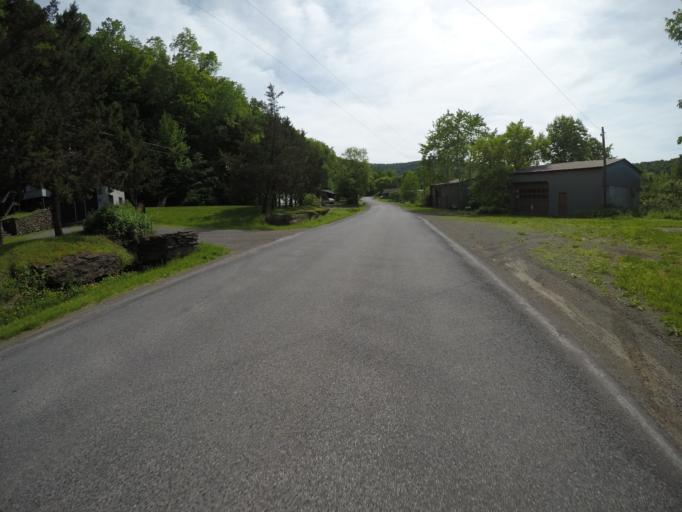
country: US
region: New York
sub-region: Sullivan County
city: Livingston Manor
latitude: 42.1270
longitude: -74.6676
